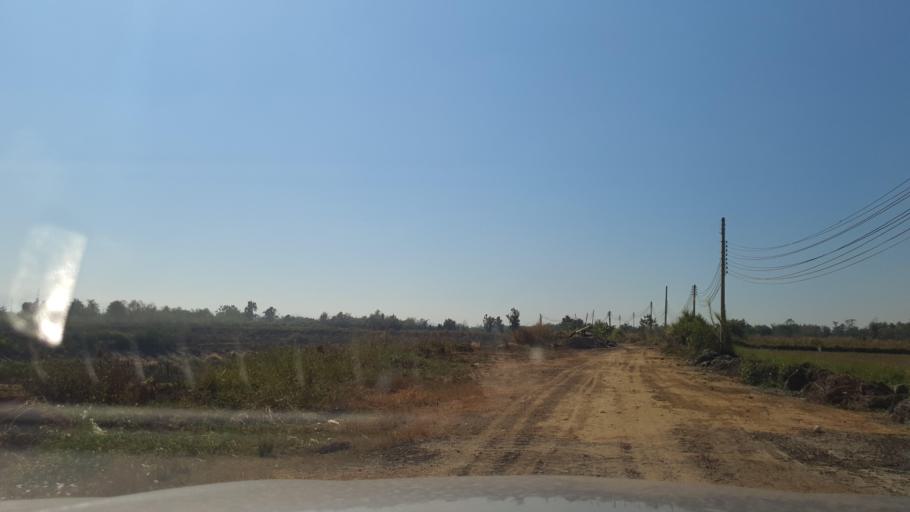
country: TH
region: Chiang Mai
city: Saraphi
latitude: 18.7160
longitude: 99.0783
